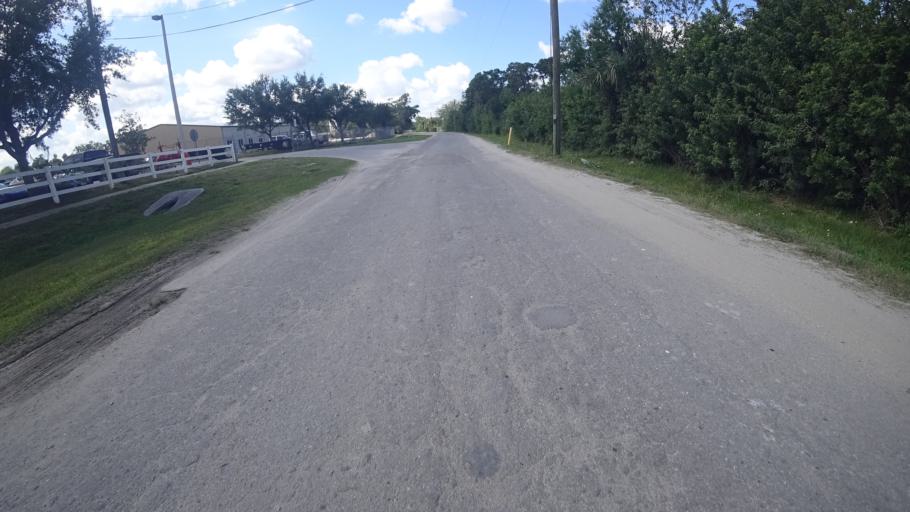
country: US
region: Florida
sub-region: Sarasota County
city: North Sarasota
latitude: 27.4094
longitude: -82.5284
